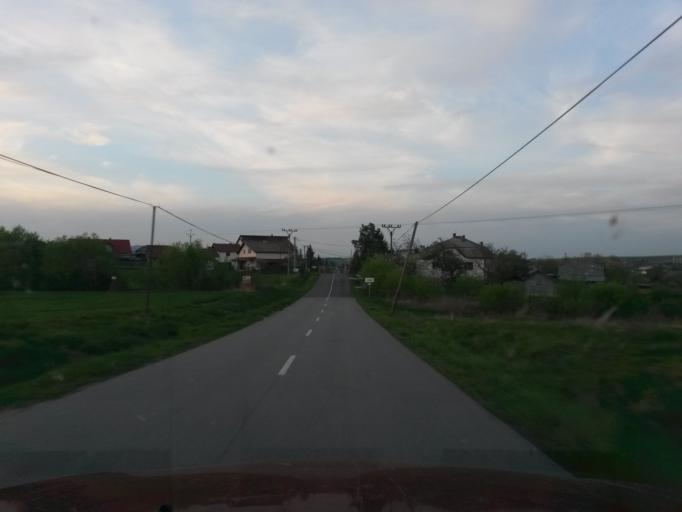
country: SK
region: Kosicky
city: Secovce
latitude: 48.5686
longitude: 21.5658
